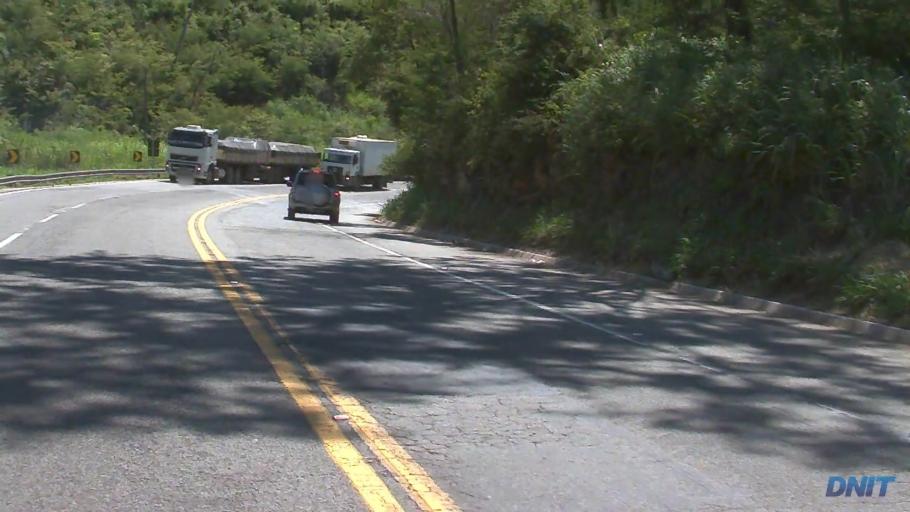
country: BR
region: Minas Gerais
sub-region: Santa Luzia
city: Santa Luzia
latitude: -19.7883
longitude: -43.7436
